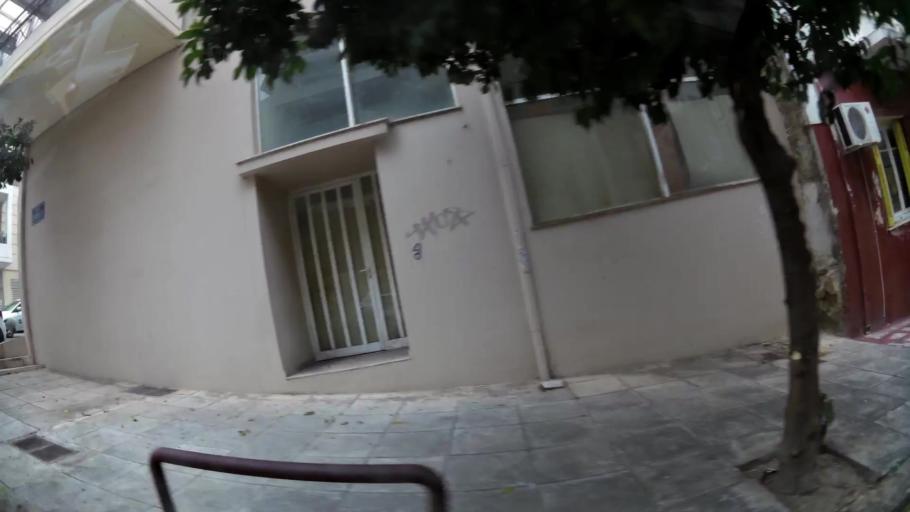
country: GR
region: Attica
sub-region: Nomos Attikis
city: Piraeus
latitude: 37.9349
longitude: 23.6376
